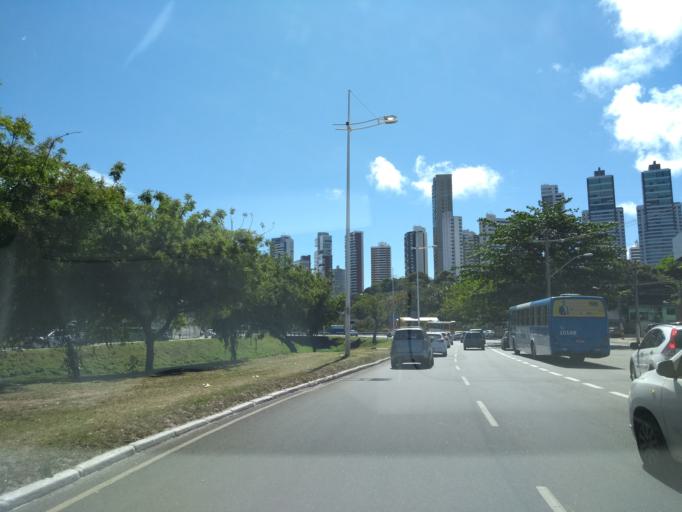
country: BR
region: Bahia
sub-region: Salvador
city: Salvador
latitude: -13.0054
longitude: -38.4856
